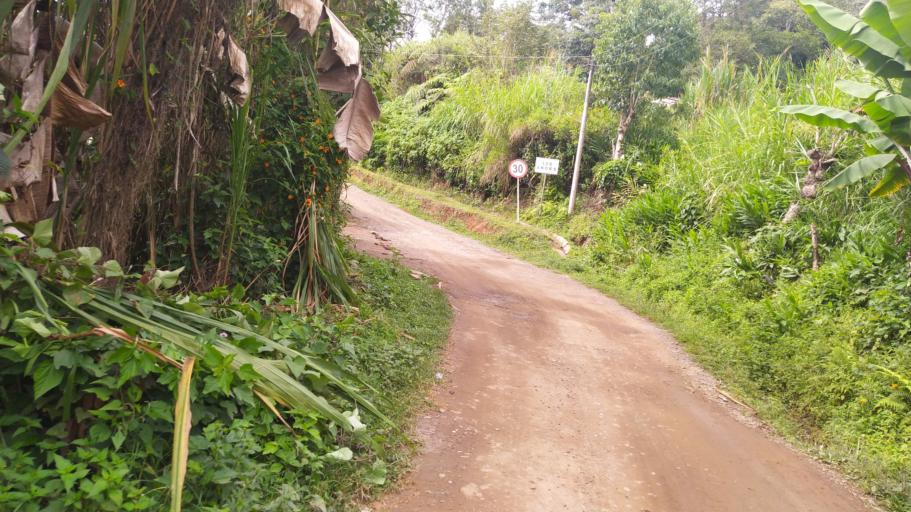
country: CO
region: Valle del Cauca
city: Cali
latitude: 3.4296
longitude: -76.6167
